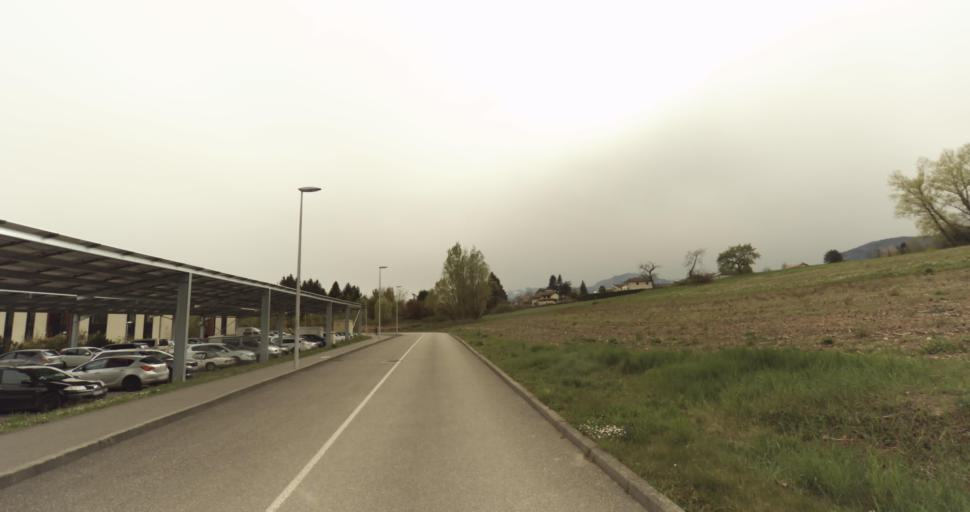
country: FR
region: Rhone-Alpes
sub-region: Departement de l'Isere
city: Montbonnot-Saint-Martin
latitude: 45.2266
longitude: 5.8191
